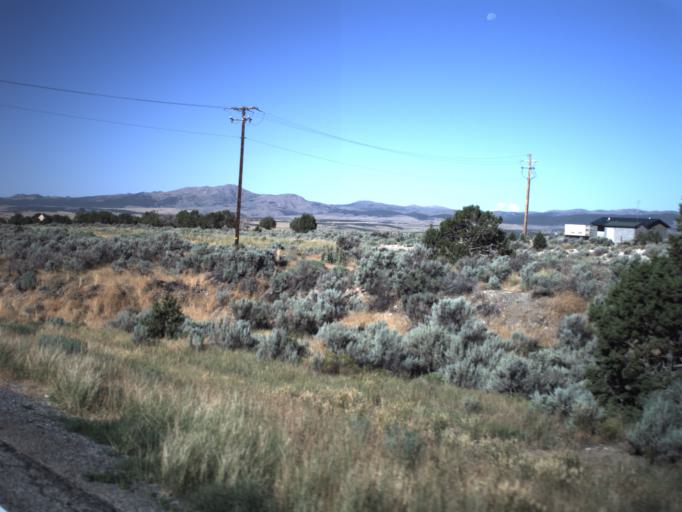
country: US
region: Utah
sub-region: Utah County
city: Genola
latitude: 39.9408
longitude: -112.1474
